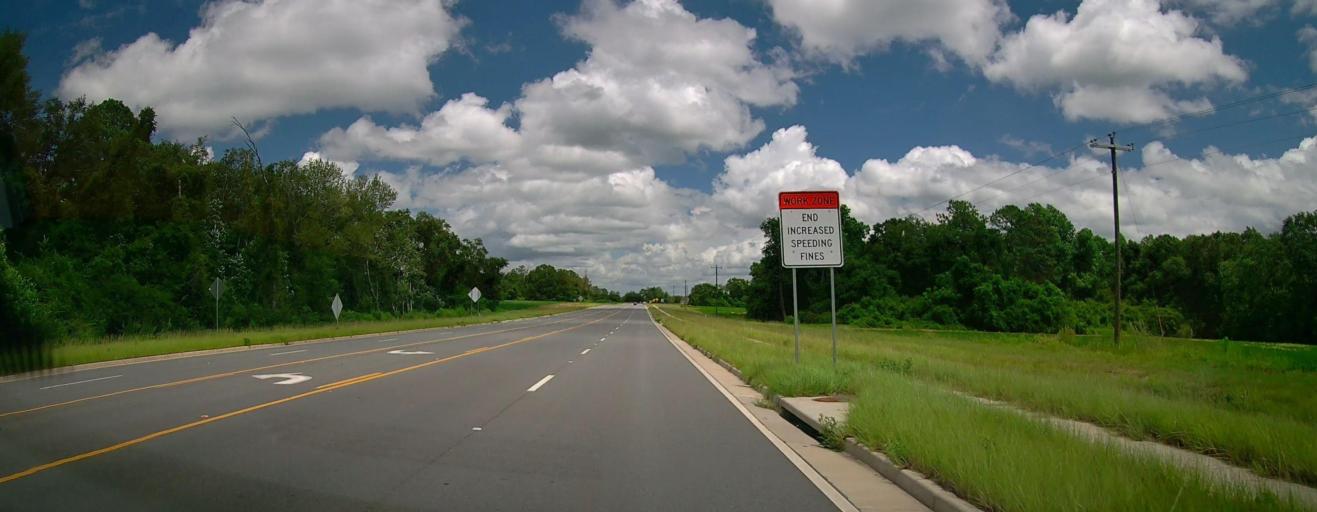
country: US
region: Georgia
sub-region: Turner County
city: Ashburn
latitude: 31.7126
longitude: -83.6340
